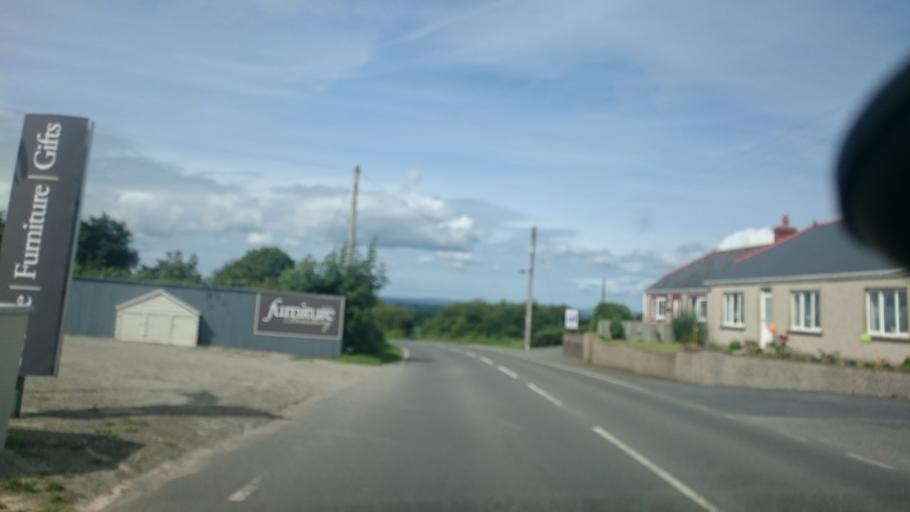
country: GB
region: Wales
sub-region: Pembrokeshire
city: Freystrop
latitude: 51.7638
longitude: -4.9606
